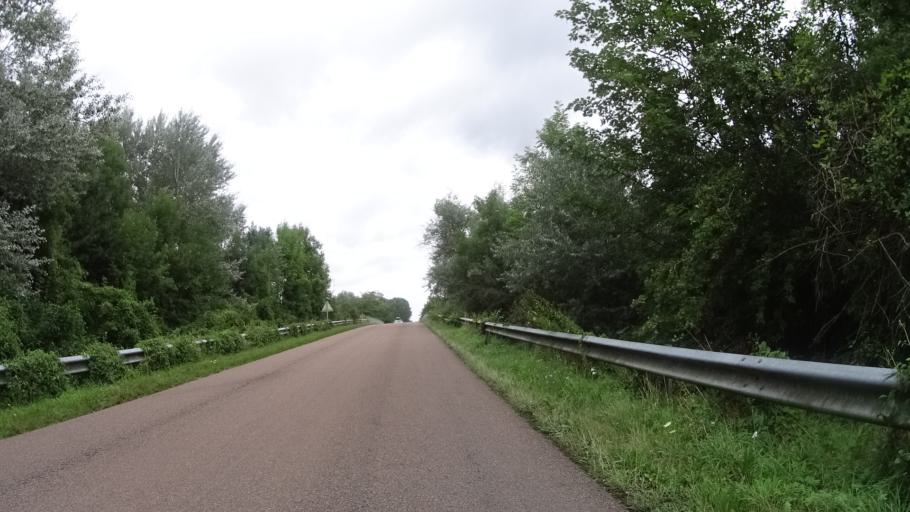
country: FR
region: Champagne-Ardenne
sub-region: Departement de l'Aube
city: Bucheres
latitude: 48.2211
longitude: 4.1236
